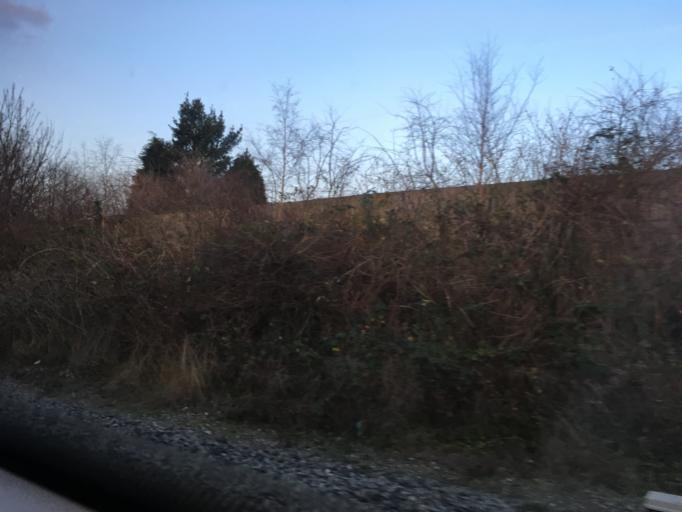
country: GB
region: England
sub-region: Manchester
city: Chorlton cum Hardy
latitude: 53.4580
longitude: -2.2798
